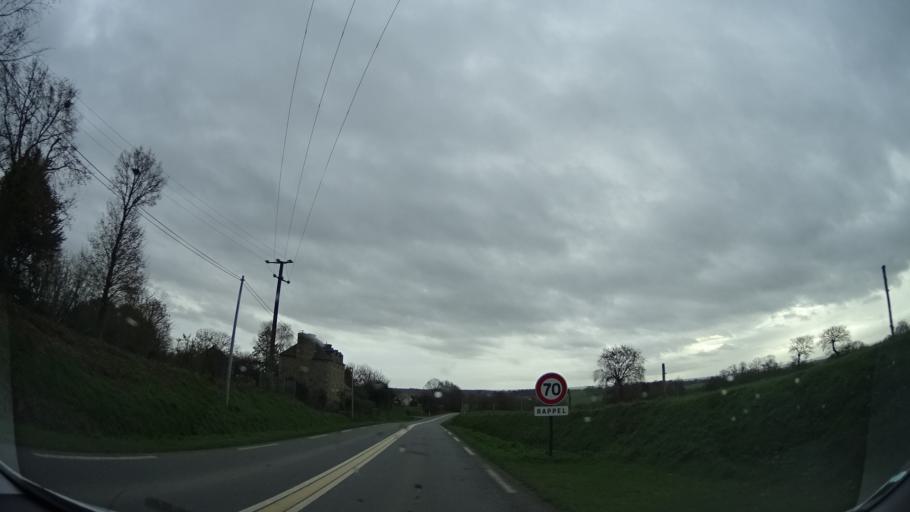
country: FR
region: Brittany
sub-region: Departement des Cotes-d'Armor
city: Les Champs-Geraux
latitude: 48.4241
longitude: -2.0047
